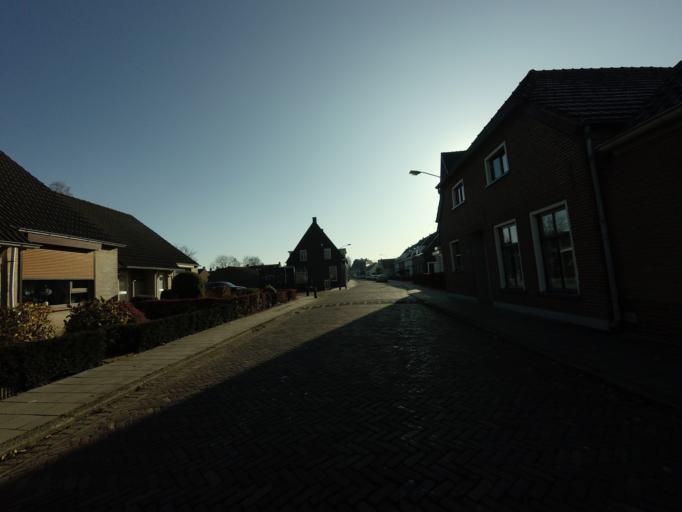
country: NL
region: Gelderland
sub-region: Gemeente Maasdriel
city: Heerewaarden
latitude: 51.7755
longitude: 5.3391
